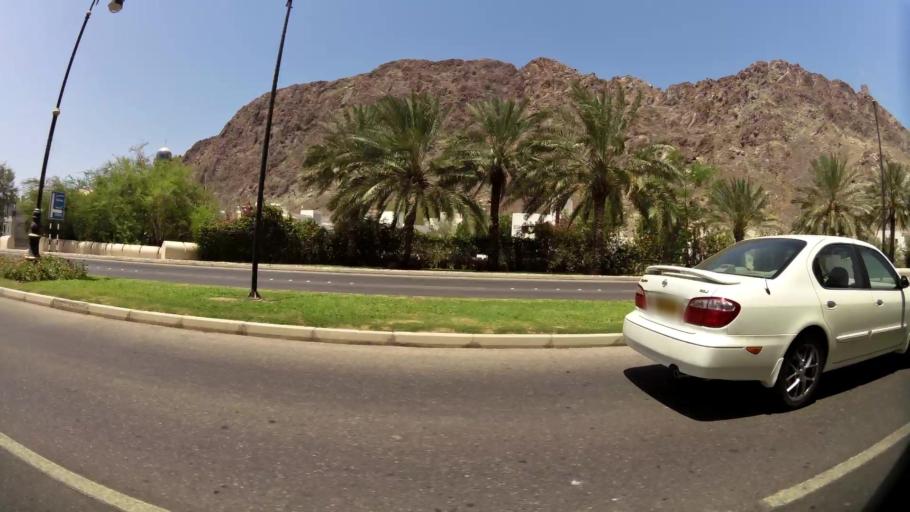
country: OM
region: Muhafazat Masqat
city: Muscat
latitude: 23.6189
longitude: 58.5865
